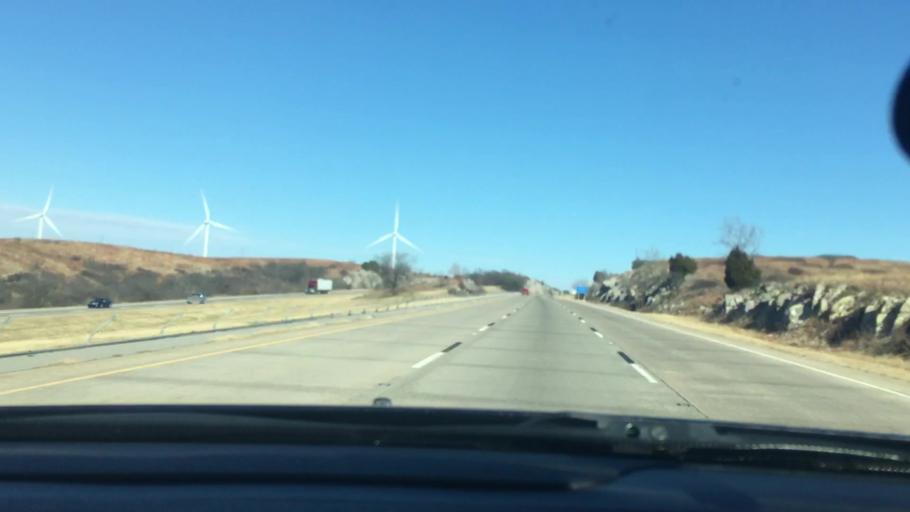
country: US
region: Oklahoma
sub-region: Murray County
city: Davis
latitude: 34.3674
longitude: -97.1461
